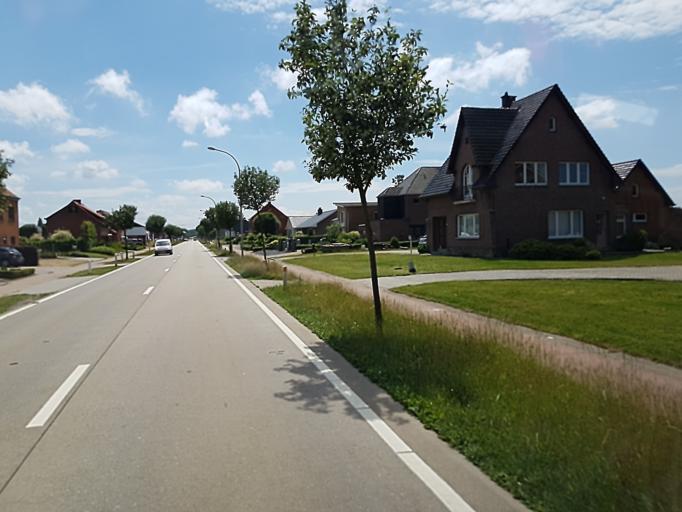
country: BE
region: Flanders
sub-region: Provincie Antwerpen
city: Westerlo
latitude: 51.1047
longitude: 4.9441
